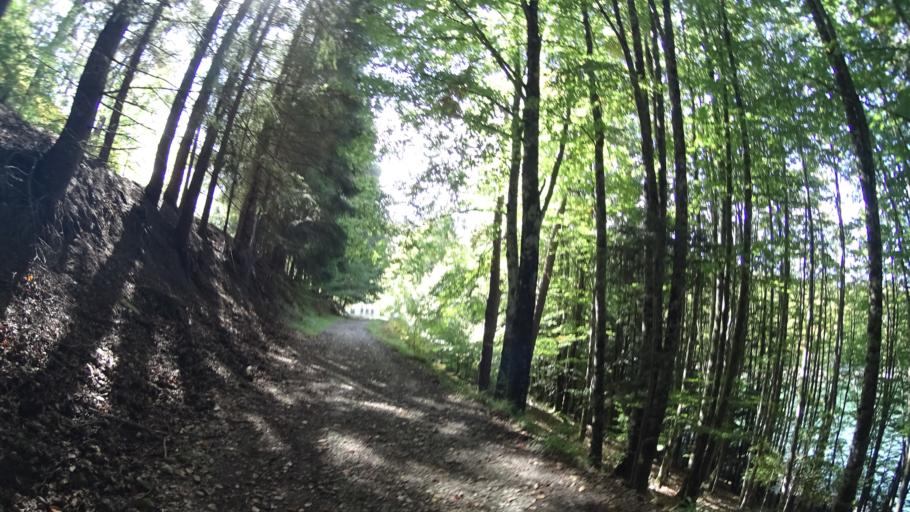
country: ES
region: Navarre
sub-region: Provincia de Navarra
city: Orbara
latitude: 42.9894
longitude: -1.1379
